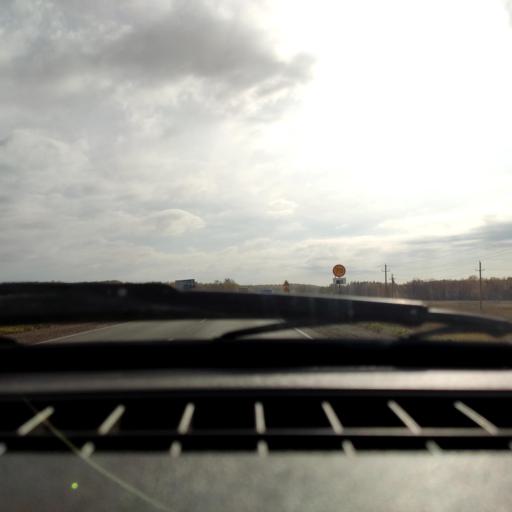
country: RU
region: Bashkortostan
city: Iglino
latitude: 54.7490
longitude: 56.2938
